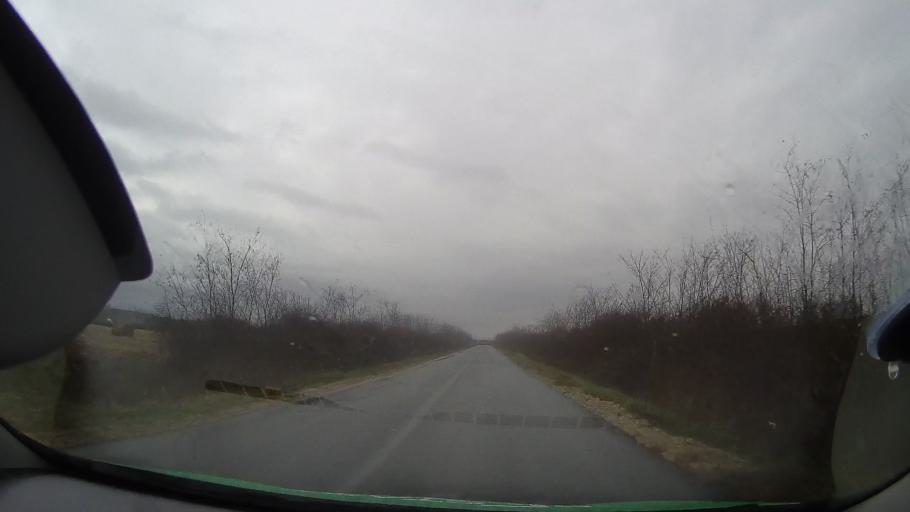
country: RO
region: Bihor
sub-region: Comuna Cociuba Mare
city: Cociuba Mare
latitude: 46.6986
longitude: 22.0329
